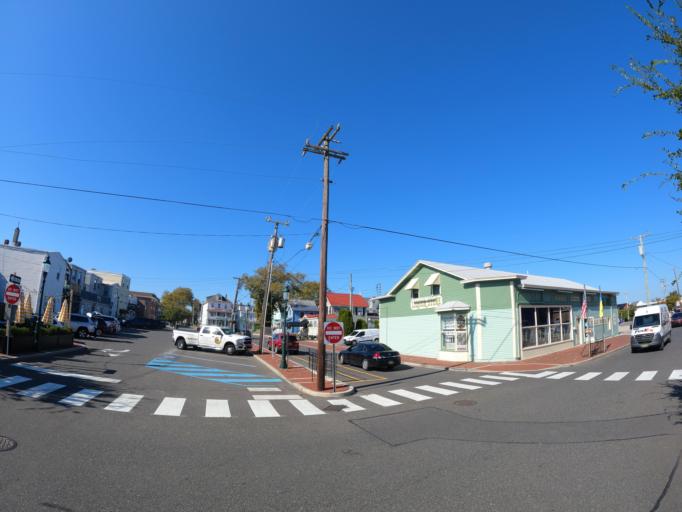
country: US
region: New Jersey
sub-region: Cape May County
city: Cape May
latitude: 38.9329
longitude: -74.9237
